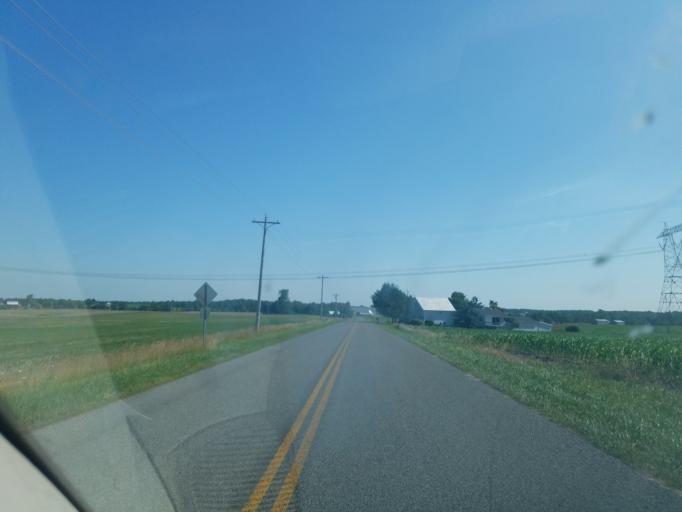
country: US
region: Ohio
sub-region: Logan County
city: Northwood
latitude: 40.4252
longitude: -83.6651
